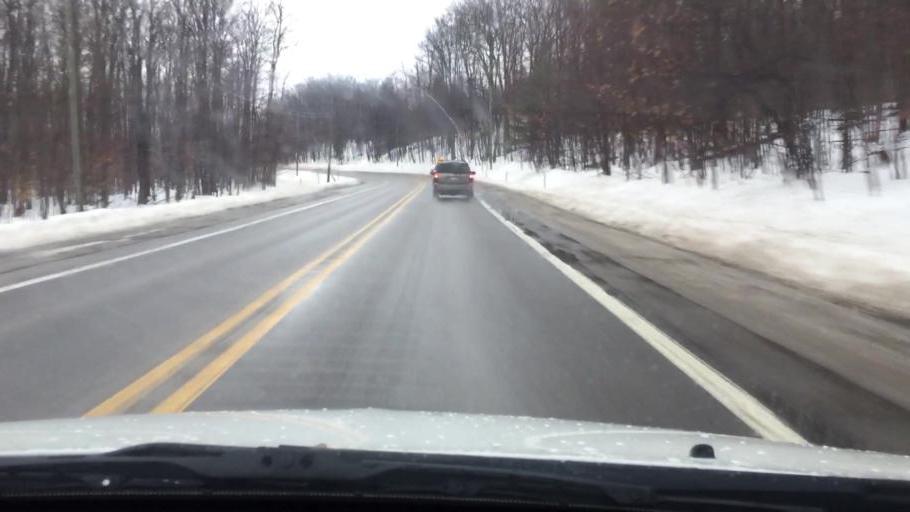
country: US
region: Michigan
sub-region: Charlevoix County
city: East Jordan
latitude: 45.2214
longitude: -85.1759
